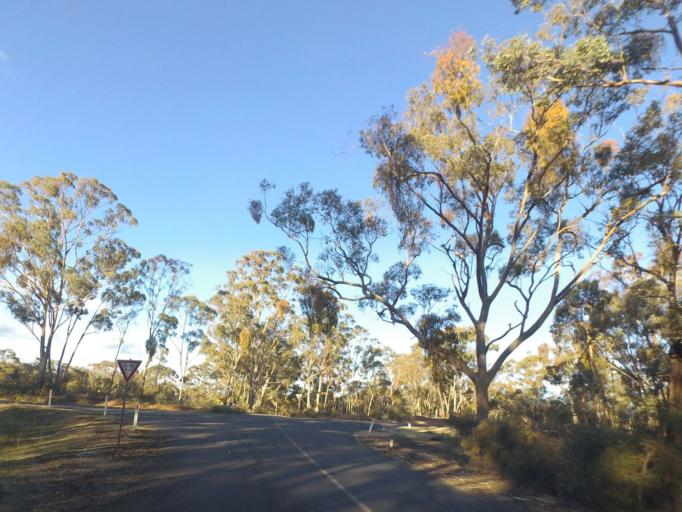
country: AU
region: Victoria
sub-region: Mount Alexander
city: Castlemaine
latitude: -37.1415
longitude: 144.2017
